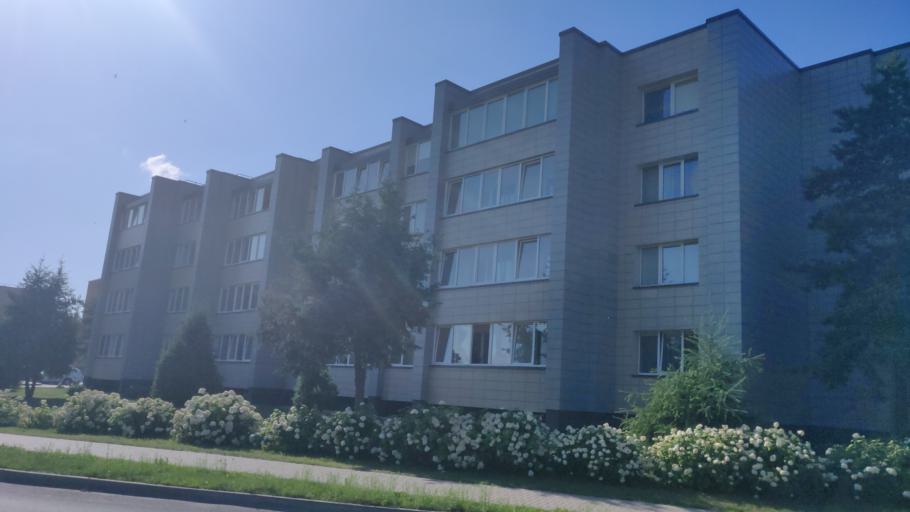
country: LT
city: Kelme
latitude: 55.6285
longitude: 22.9412
